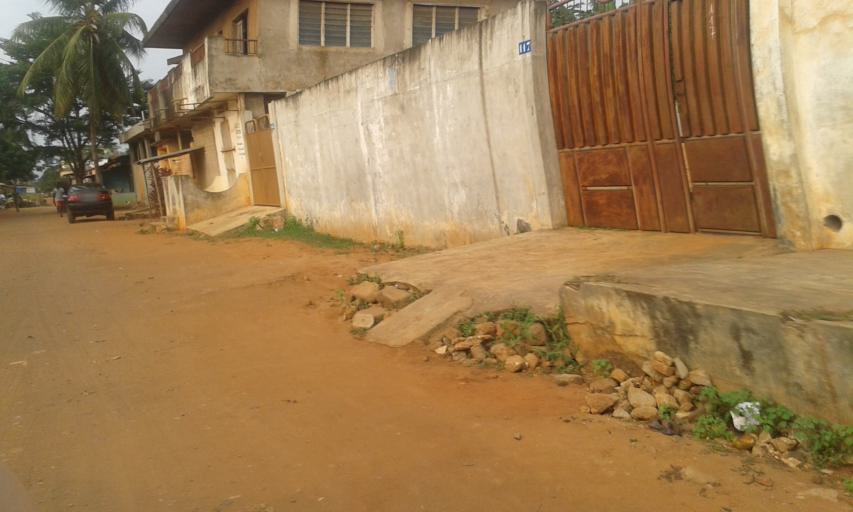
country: BJ
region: Queme
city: Porto-Novo
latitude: 6.4775
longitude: 2.6101
